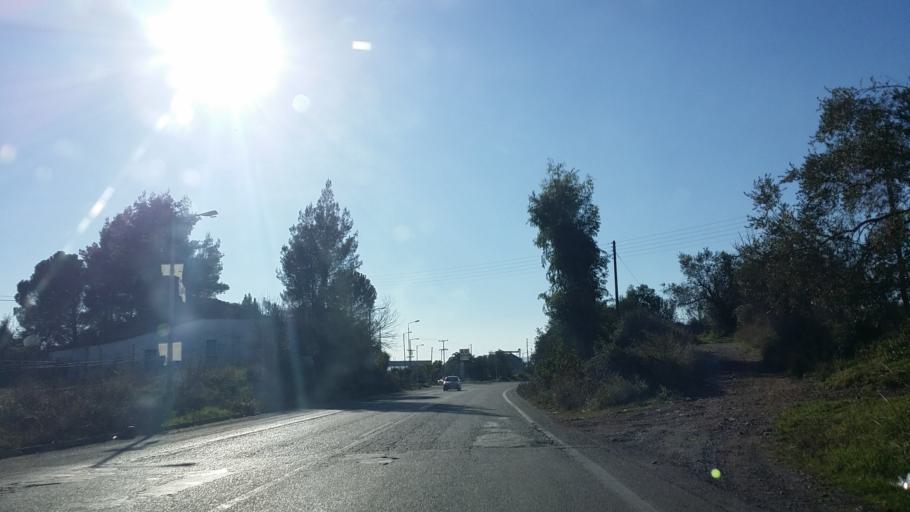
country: GR
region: West Greece
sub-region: Nomos Aitolias kai Akarnanias
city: Neapolis
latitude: 38.6718
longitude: 21.3482
